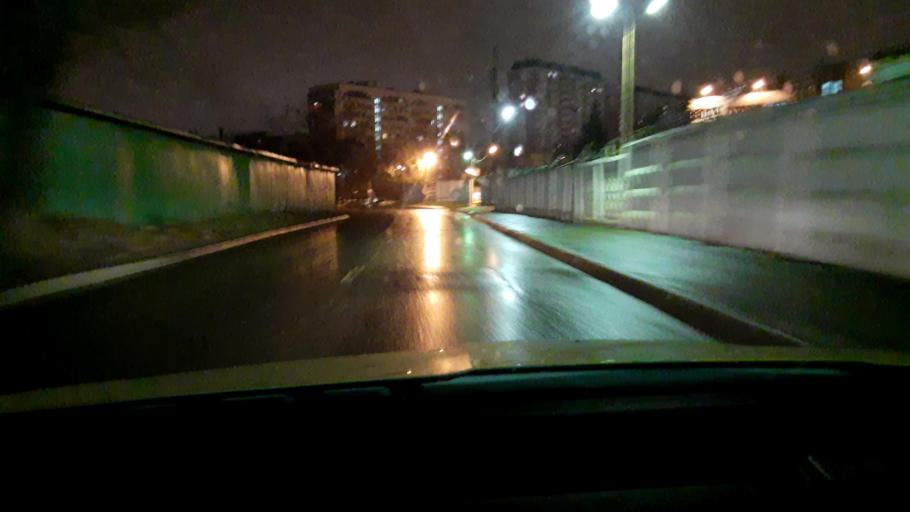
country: RU
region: Moscow
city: Kozeyevo
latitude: 55.8945
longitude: 37.6452
